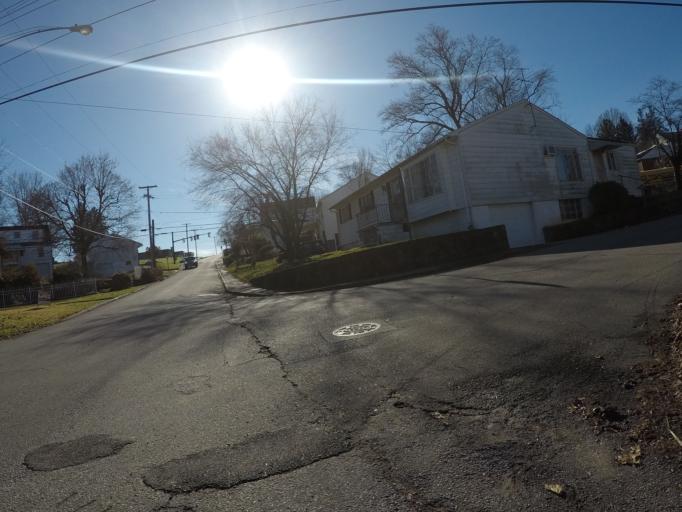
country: US
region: West Virginia
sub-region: Cabell County
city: Huntington
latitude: 38.4070
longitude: -82.4011
